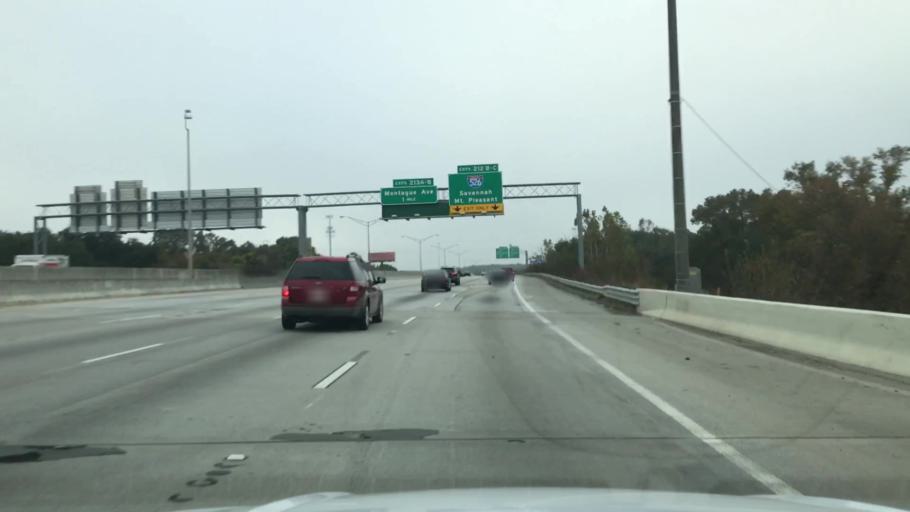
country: US
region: South Carolina
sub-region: Berkeley County
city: Hanahan
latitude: 32.8924
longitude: -80.0188
